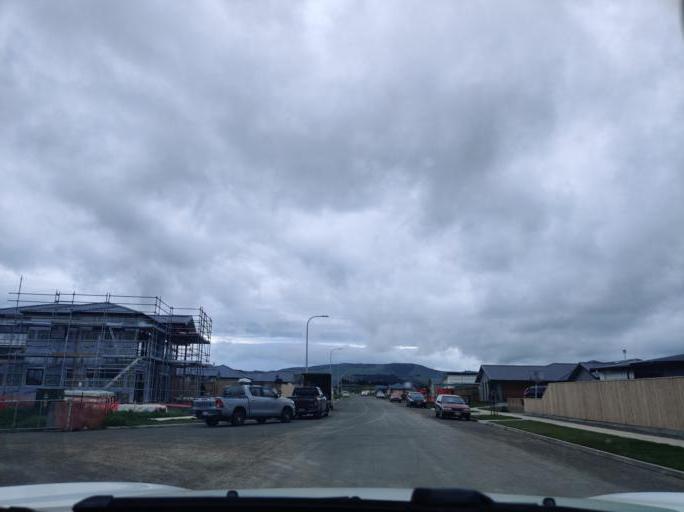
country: NZ
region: Manawatu-Wanganui
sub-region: Palmerston North City
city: Palmerston North
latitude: -40.3867
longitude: 175.6471
